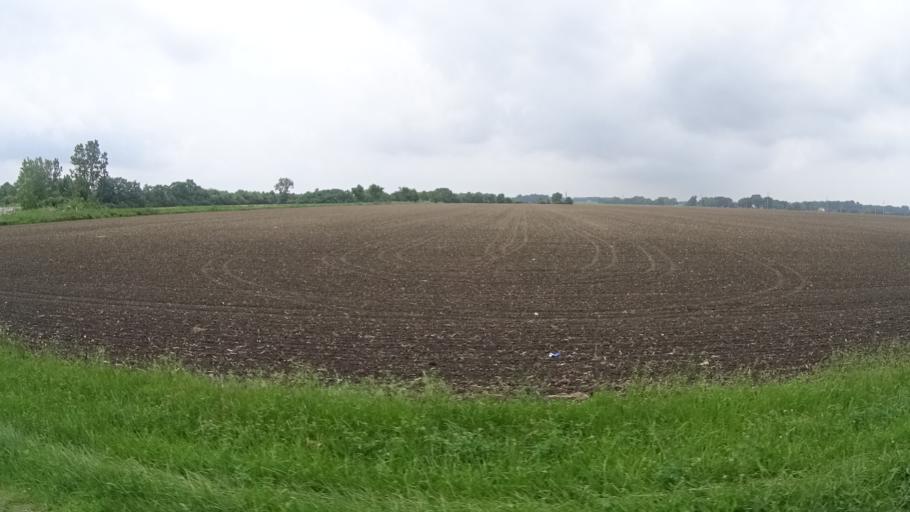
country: US
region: Ohio
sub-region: Huron County
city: Bellevue
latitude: 41.3384
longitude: -82.7938
